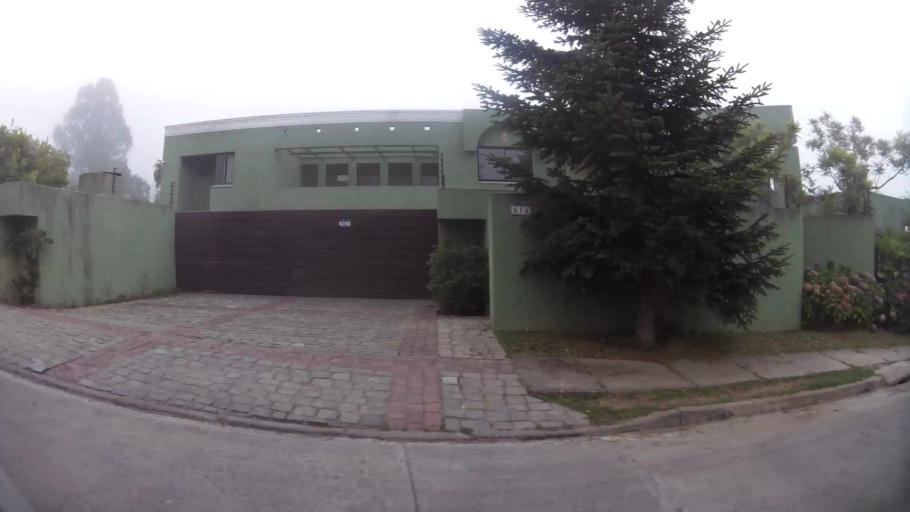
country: CL
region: Biobio
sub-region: Provincia de Concepcion
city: Concepcion
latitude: -36.8273
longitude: -73.0287
